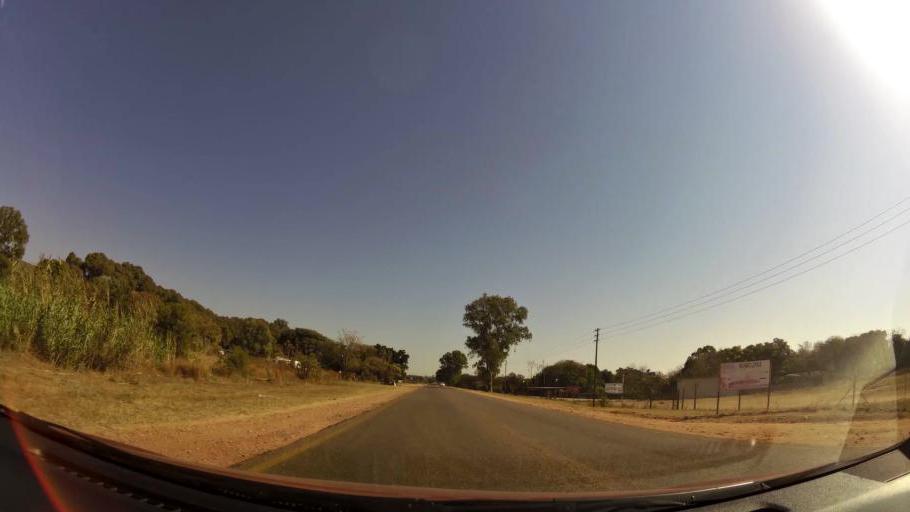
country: ZA
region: North-West
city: Ga-Rankuwa
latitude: -25.6655
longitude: 28.0717
